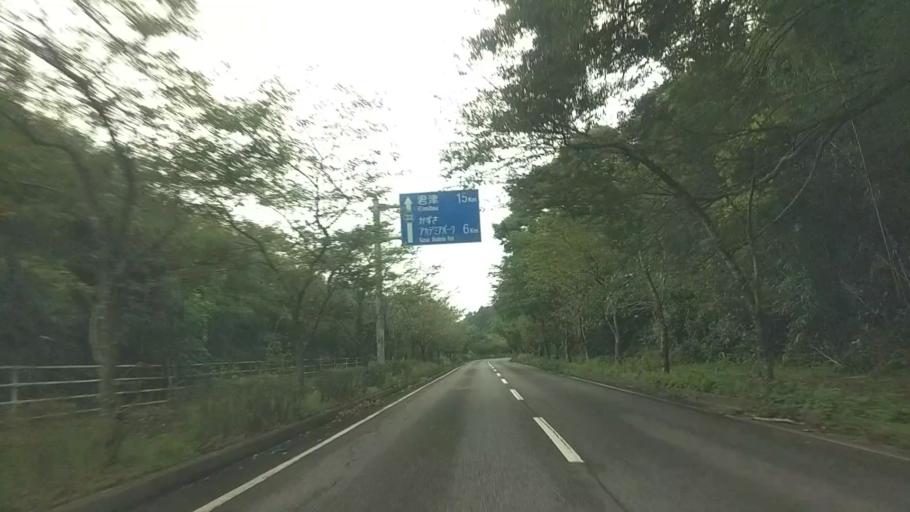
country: JP
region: Chiba
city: Kisarazu
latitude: 35.3836
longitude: 140.0067
